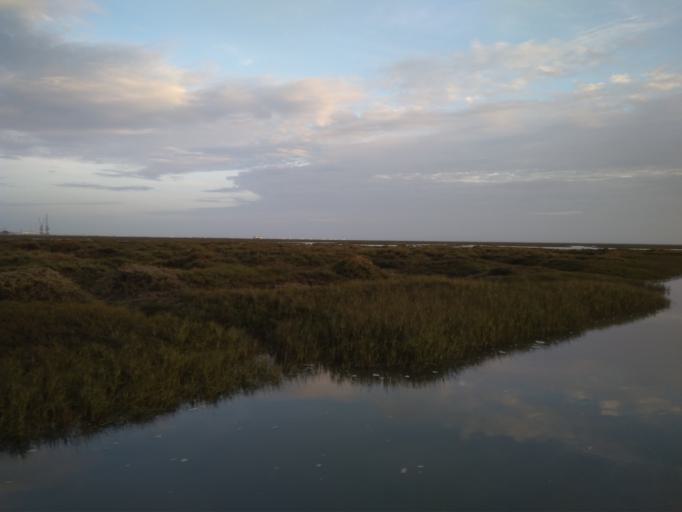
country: PT
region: Faro
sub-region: Faro
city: Faro
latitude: 37.0041
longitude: -7.9356
